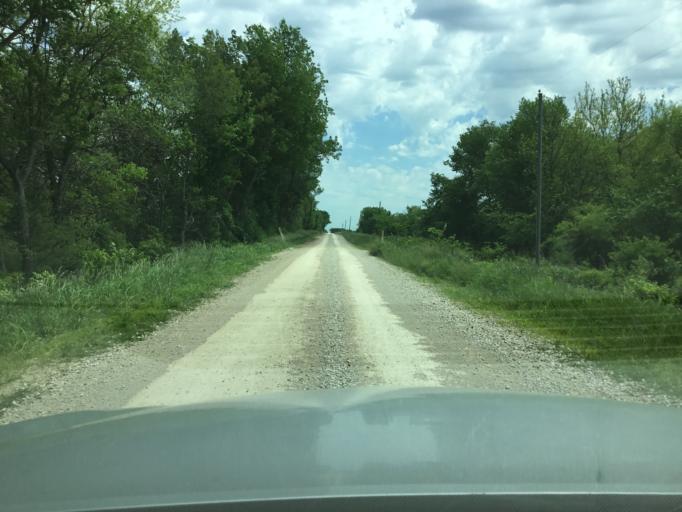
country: US
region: Kansas
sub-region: Montgomery County
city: Independence
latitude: 37.0952
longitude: -95.7909
